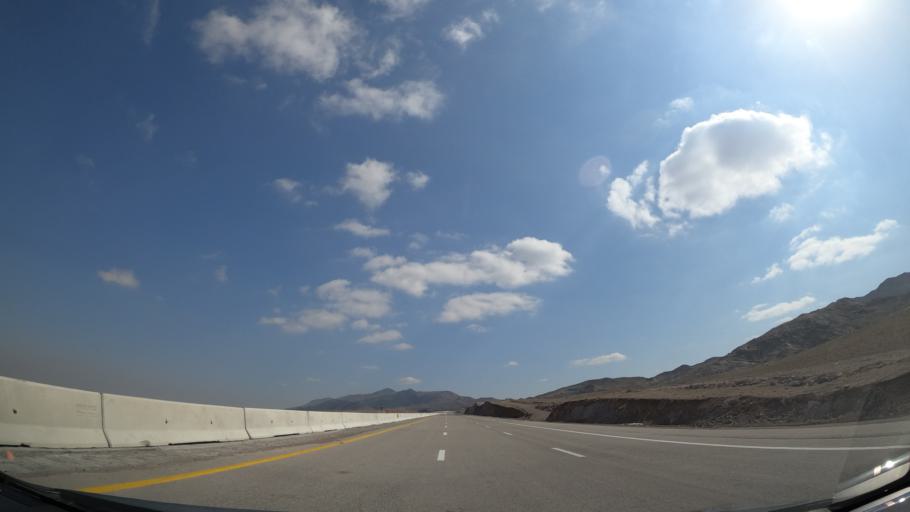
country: IR
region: Alborz
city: Nazarabad
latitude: 35.7006
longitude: 50.6207
